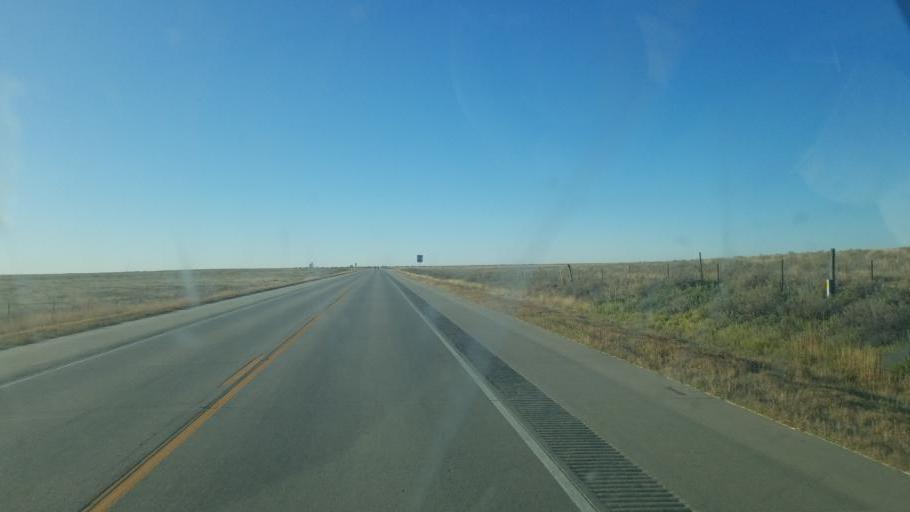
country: US
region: Colorado
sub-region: Kiowa County
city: Eads
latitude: 38.5264
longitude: -102.7858
